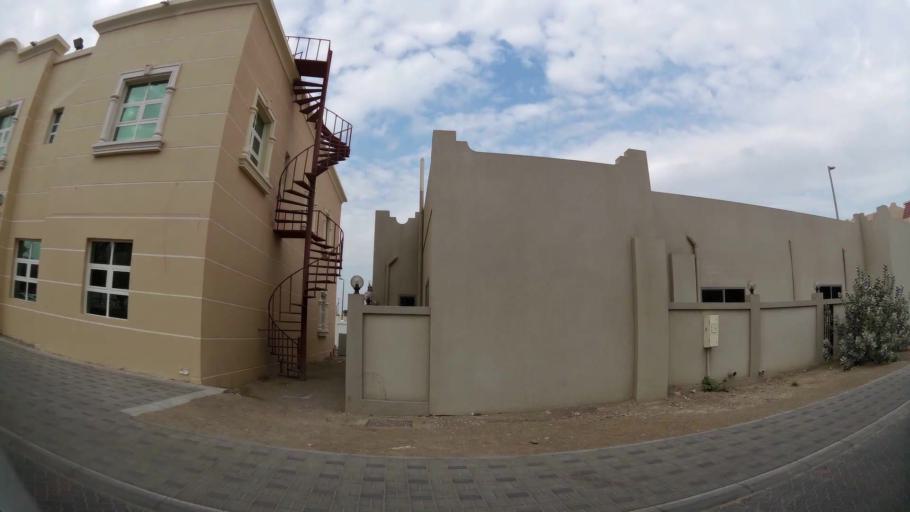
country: AE
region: Abu Dhabi
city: Al Ain
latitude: 24.2263
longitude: 55.7378
